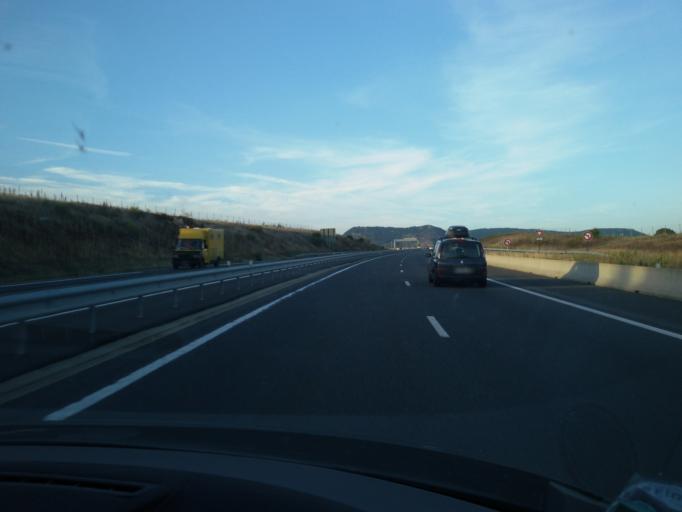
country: FR
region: Midi-Pyrenees
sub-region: Departement de l'Aveyron
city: Creissels
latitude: 44.1014
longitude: 3.0233
